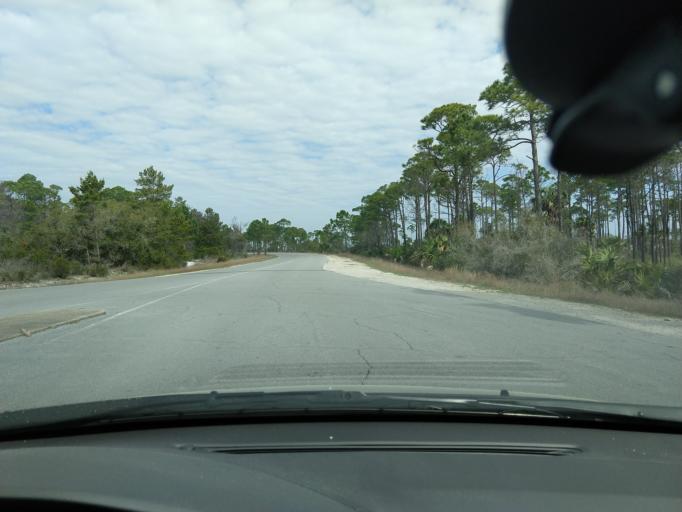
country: US
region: Florida
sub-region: Gulf County
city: Port Saint Joe
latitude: 29.7587
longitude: -85.3966
